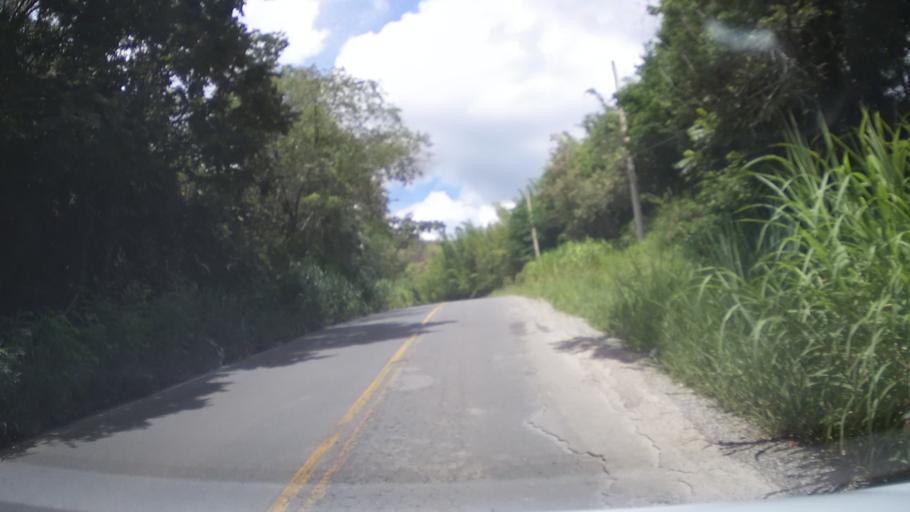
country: BR
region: Sao Paulo
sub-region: Valinhos
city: Valinhos
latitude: -22.9761
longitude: -46.9611
